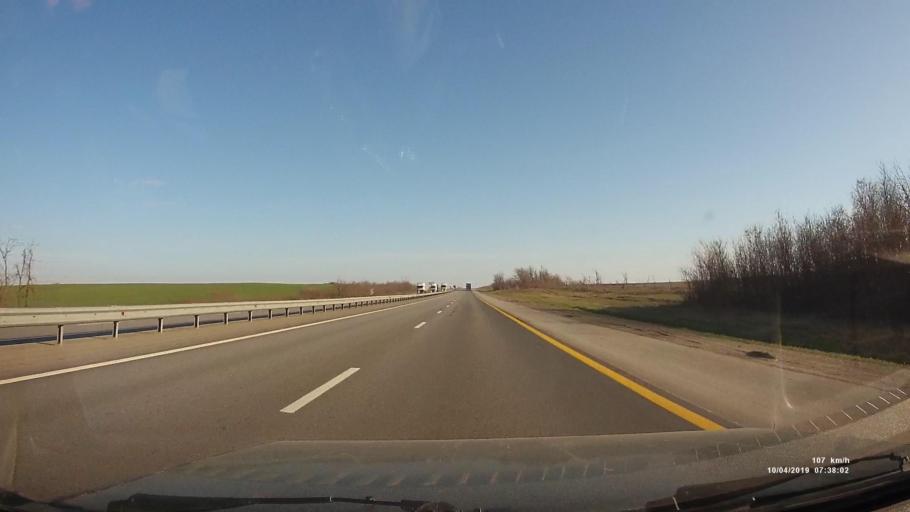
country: RU
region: Rostov
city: Likhoy
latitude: 48.0825
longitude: 40.2596
